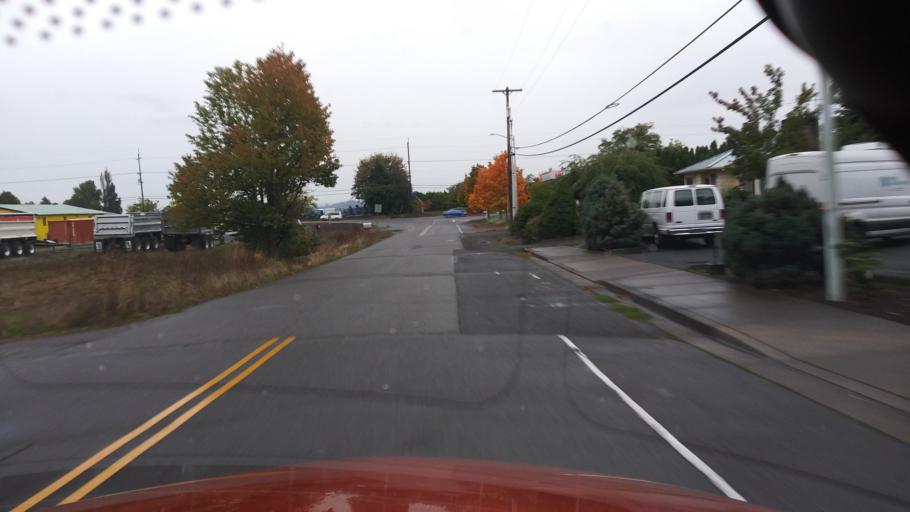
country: US
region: Oregon
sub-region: Washington County
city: Cornelius
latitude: 45.5214
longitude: -123.0359
